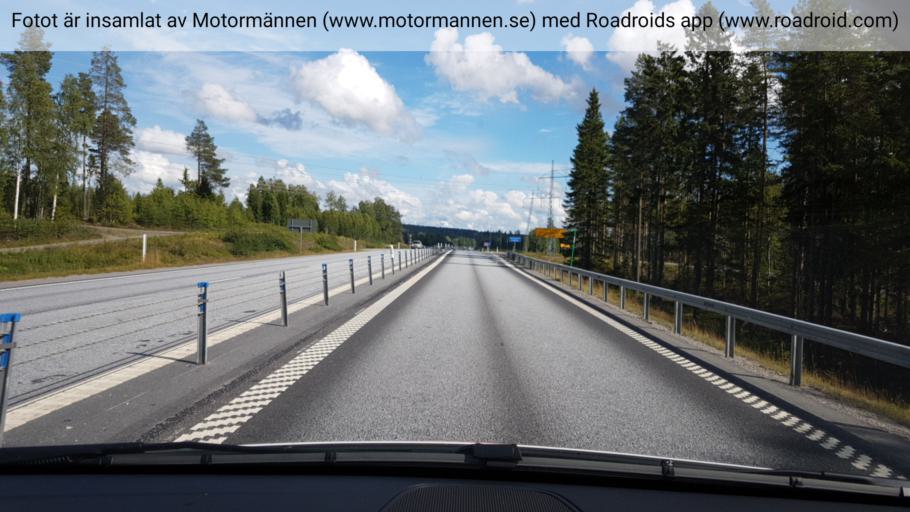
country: SE
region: Vaesterbotten
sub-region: Vannas Kommun
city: Vannasby
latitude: 63.8940
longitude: 19.9404
